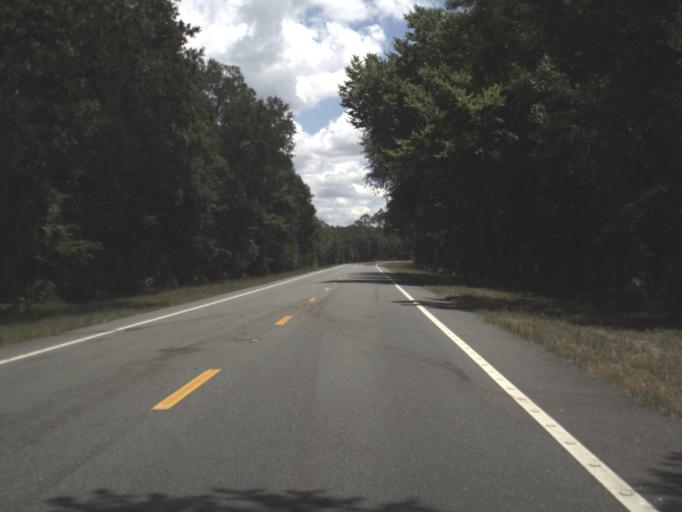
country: US
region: Florida
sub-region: Leon County
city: Woodville
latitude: 30.1442
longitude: -83.9499
